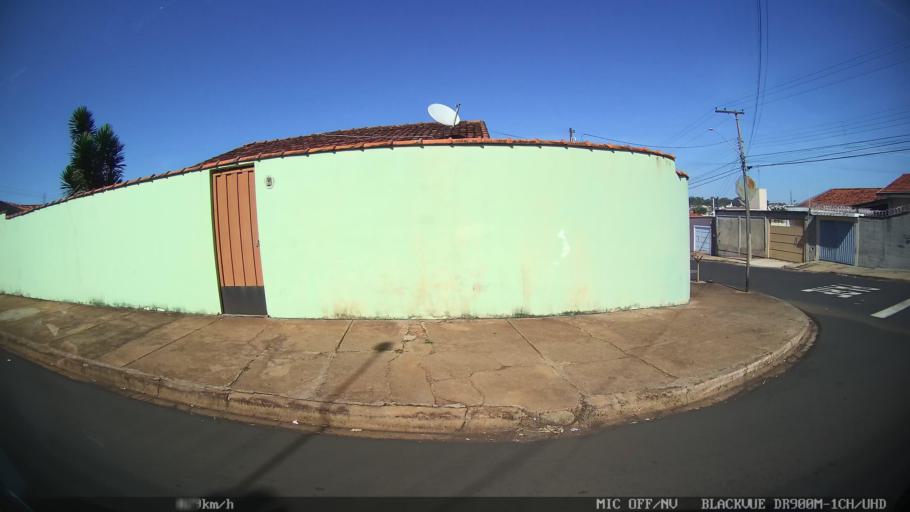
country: BR
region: Sao Paulo
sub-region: Batatais
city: Batatais
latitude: -20.8889
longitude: -47.5749
